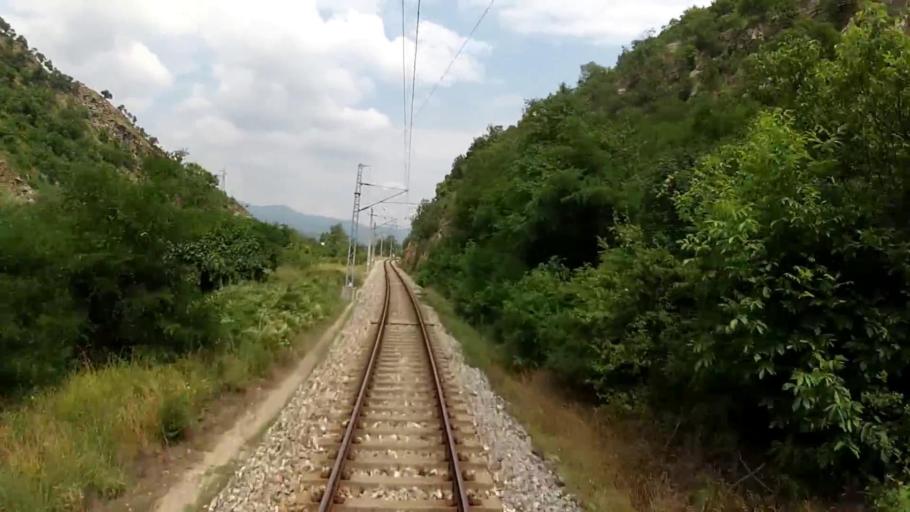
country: BG
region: Blagoevgrad
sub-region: Obshtina Kresna
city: Stara Kresna
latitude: 41.8342
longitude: 23.1557
